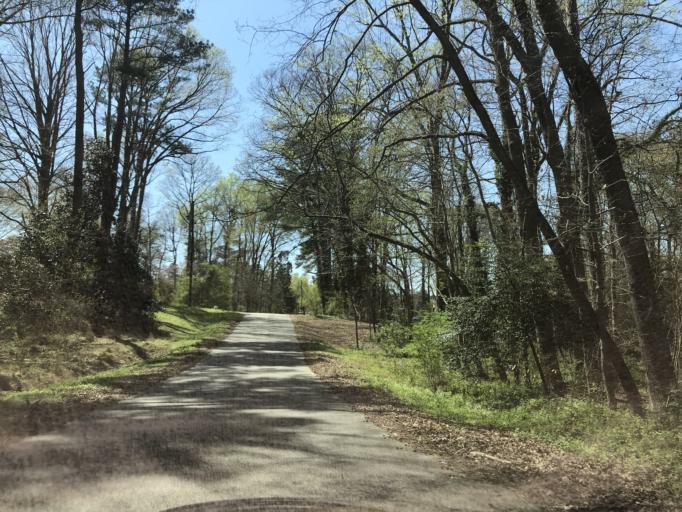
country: US
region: North Carolina
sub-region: Wake County
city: Raleigh
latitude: 35.8147
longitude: -78.5758
